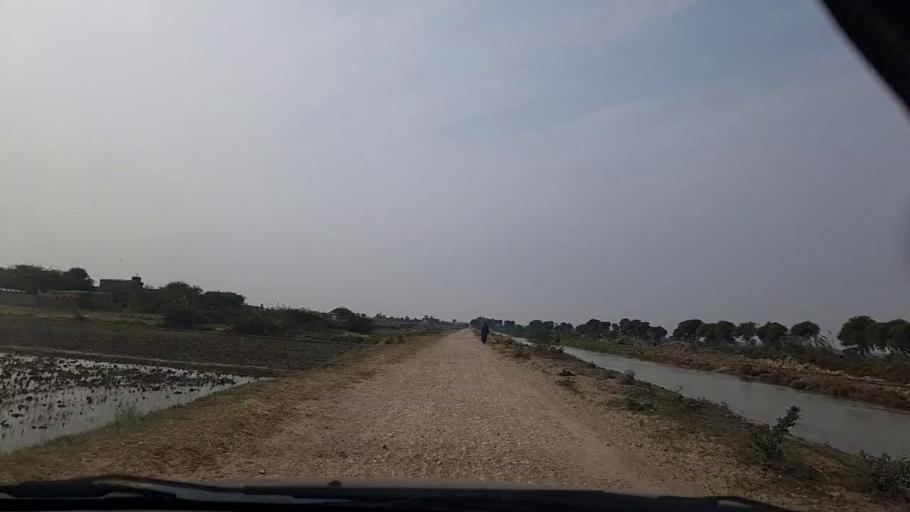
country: PK
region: Sindh
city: Thatta
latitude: 24.5782
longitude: 67.8901
